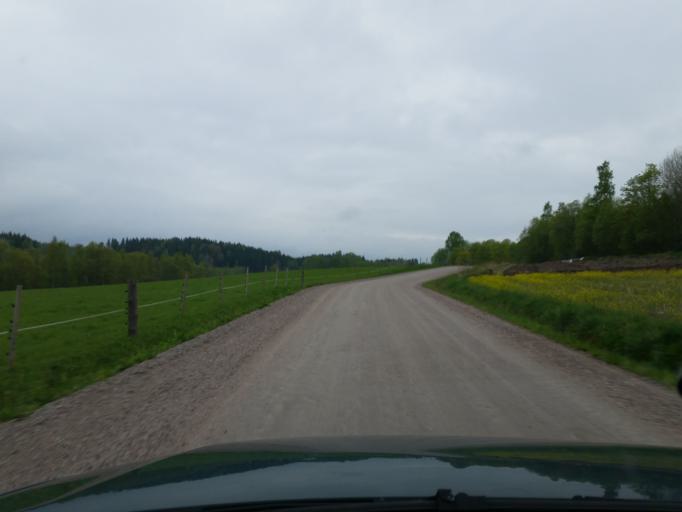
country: FI
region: Uusimaa
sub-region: Helsinki
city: Karjalohja
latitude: 60.1850
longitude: 23.6841
